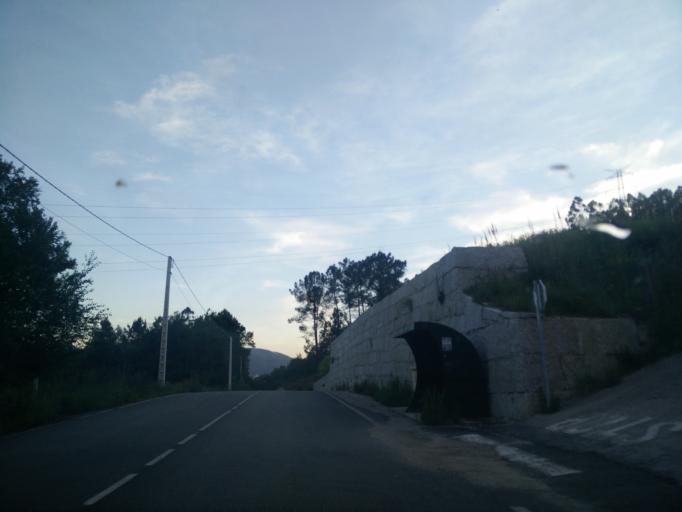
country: ES
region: Galicia
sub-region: Provincia de Pontevedra
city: Mondariz
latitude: 42.2491
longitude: -8.4380
